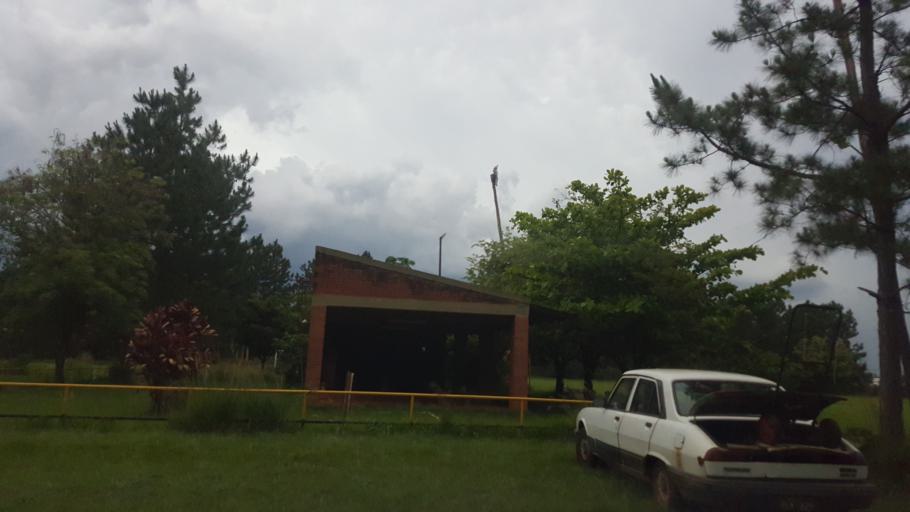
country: AR
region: Misiones
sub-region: Departamento de Capital
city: Posadas
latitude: -27.4003
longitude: -55.9744
